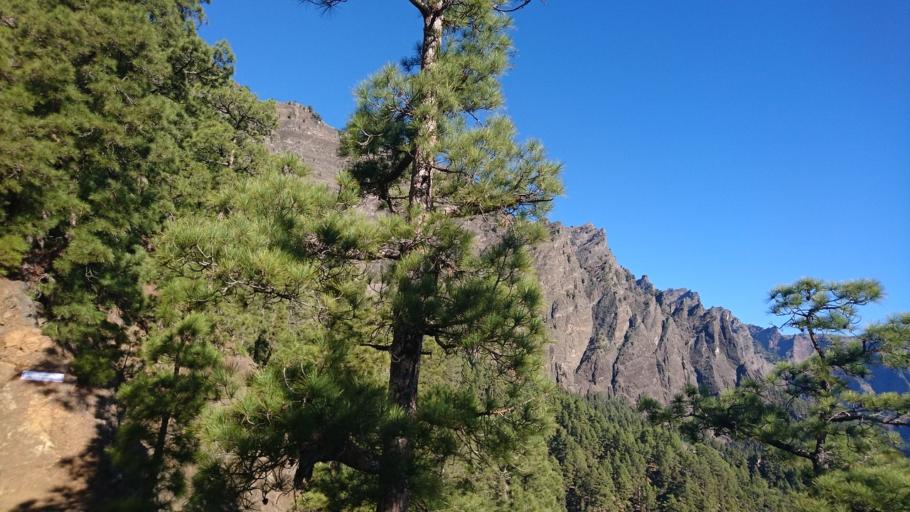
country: ES
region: Canary Islands
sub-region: Provincia de Santa Cruz de Tenerife
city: Tijarafe
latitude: 28.7117
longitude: -17.9007
